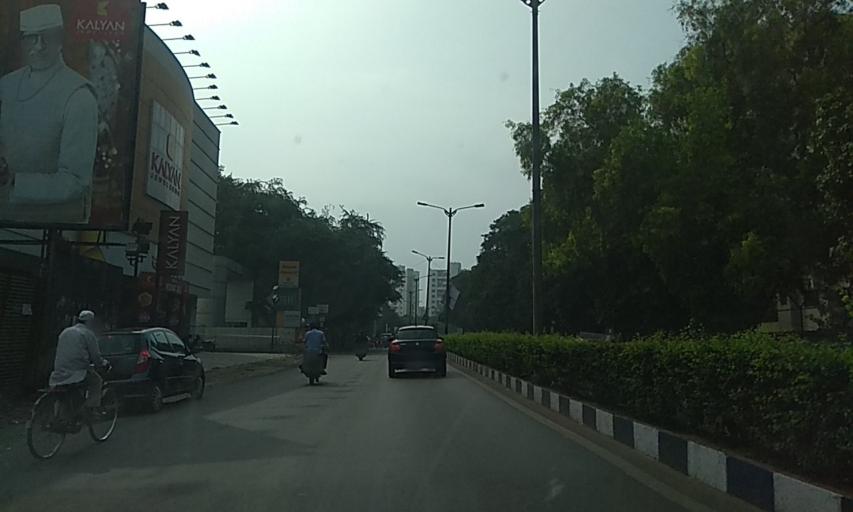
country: IN
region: Maharashtra
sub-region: Pune Division
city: Pune
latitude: 18.5128
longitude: 73.9325
